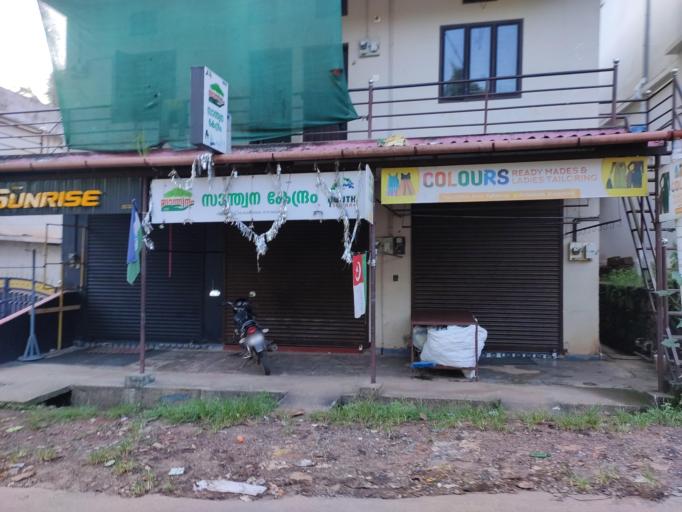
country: IN
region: Kerala
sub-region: Palakkad district
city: Mannarakkat
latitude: 10.9656
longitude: 76.4752
